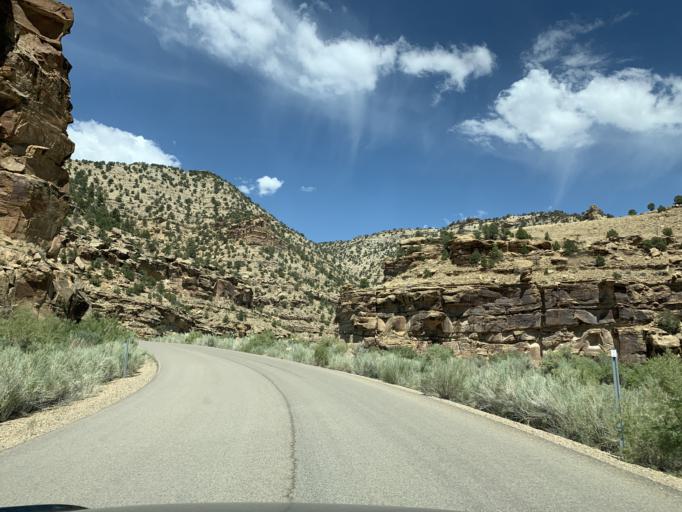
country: US
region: Utah
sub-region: Carbon County
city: East Carbon City
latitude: 39.8157
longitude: -110.2519
